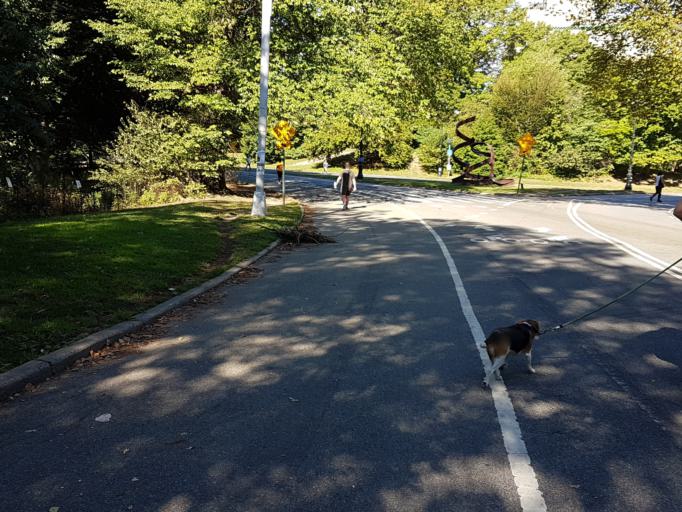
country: US
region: New York
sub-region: Kings County
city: Brooklyn
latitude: 40.6710
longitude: -73.9690
